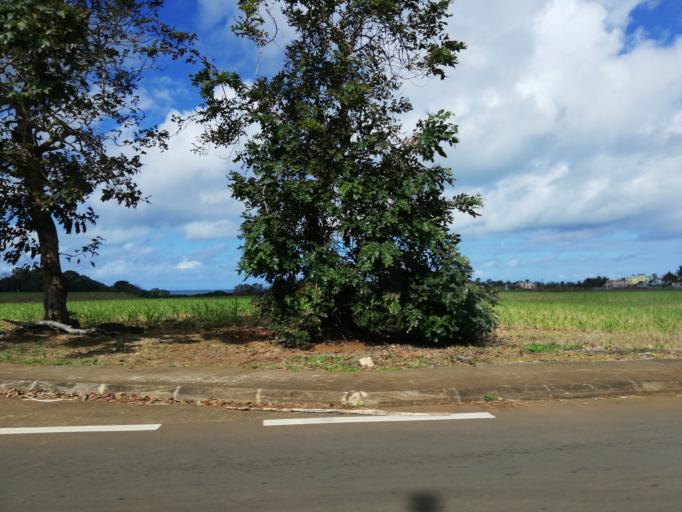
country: MU
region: Grand Port
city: Mahebourg
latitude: -20.3853
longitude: 57.6967
